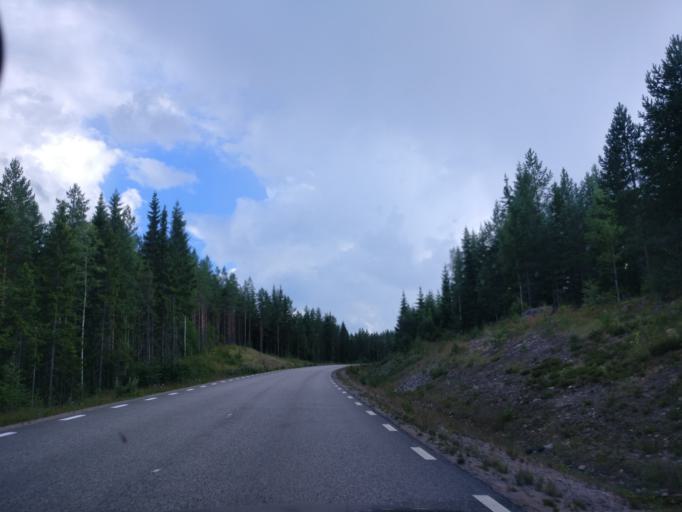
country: SE
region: Dalarna
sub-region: Ludvika Kommun
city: Abborrberget
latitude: 60.1777
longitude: 14.6730
